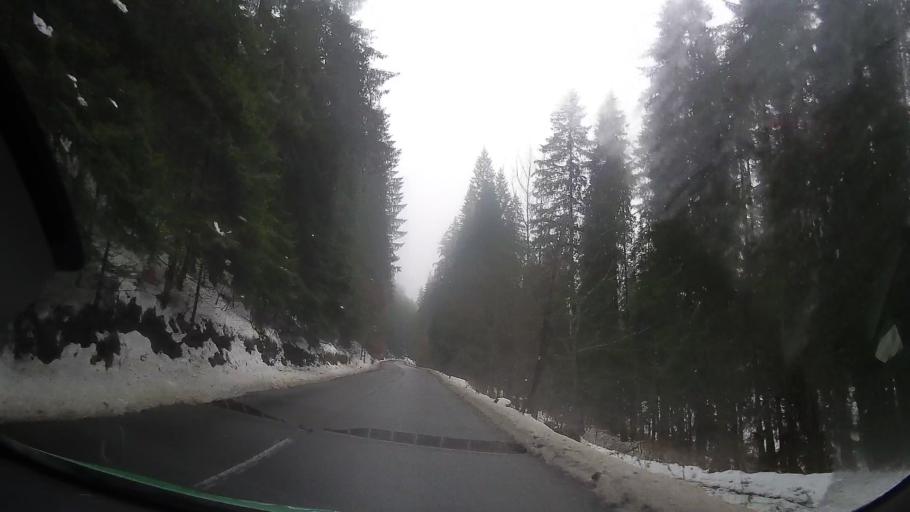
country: RO
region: Neamt
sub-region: Comuna Bicaz Chei
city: Bicaz Chei
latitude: 46.7864
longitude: 25.7876
